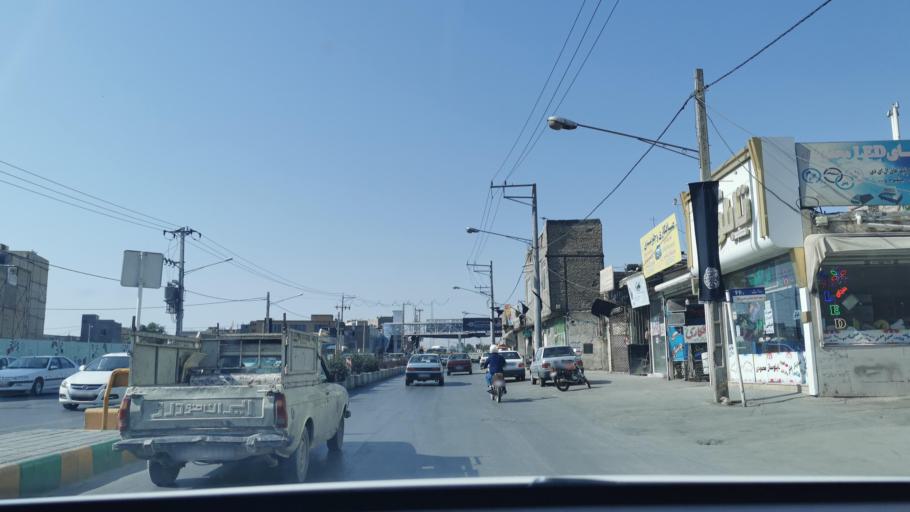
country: IR
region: Razavi Khorasan
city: Mashhad
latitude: 36.3234
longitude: 59.6413
